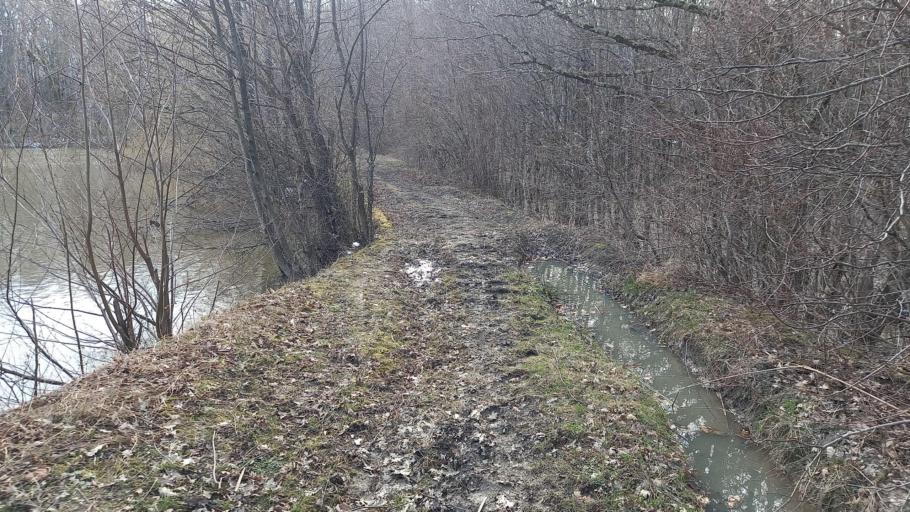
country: RU
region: Krasnodarskiy
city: Smolenskaya
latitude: 44.5956
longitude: 38.8462
